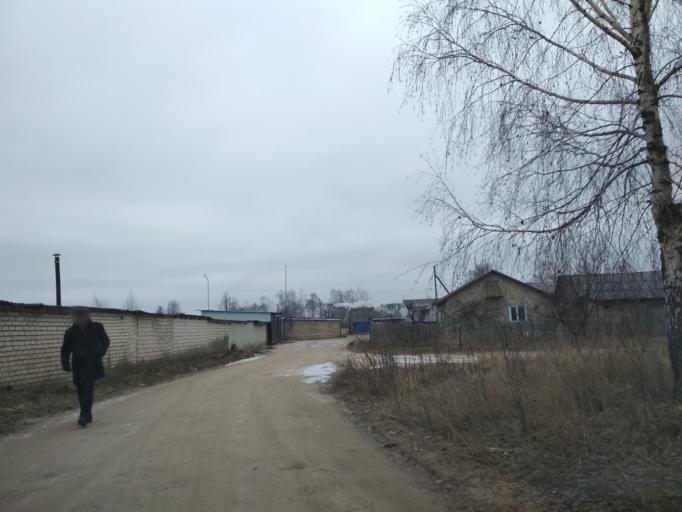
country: BY
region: Minsk
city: Mar''ina Horka
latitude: 53.5025
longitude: 28.1530
